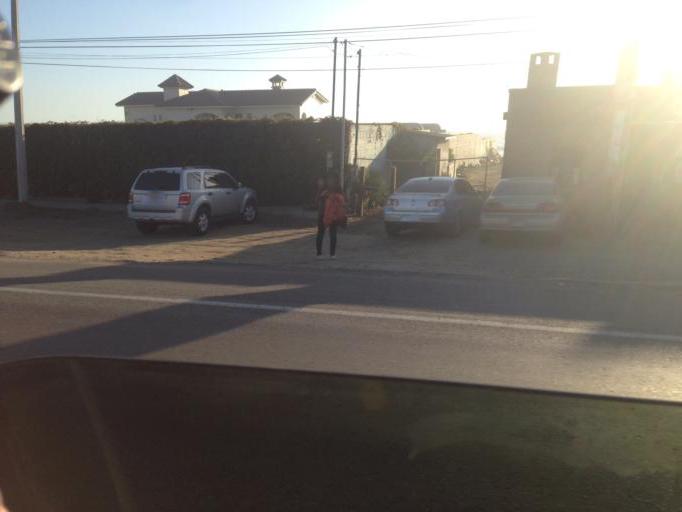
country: MX
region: Baja California
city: El Sauzal
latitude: 31.8892
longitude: -116.6912
